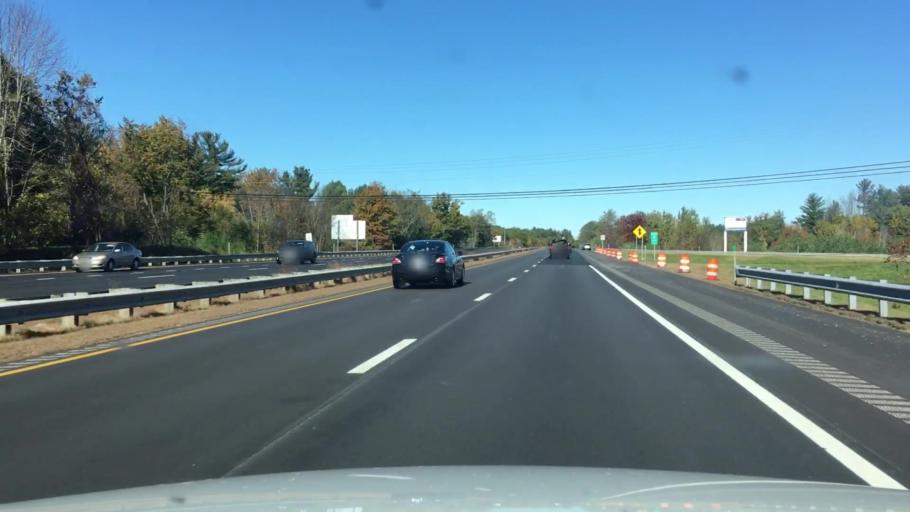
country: US
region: New Hampshire
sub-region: Strafford County
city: Dover
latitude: 43.1871
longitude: -70.8886
